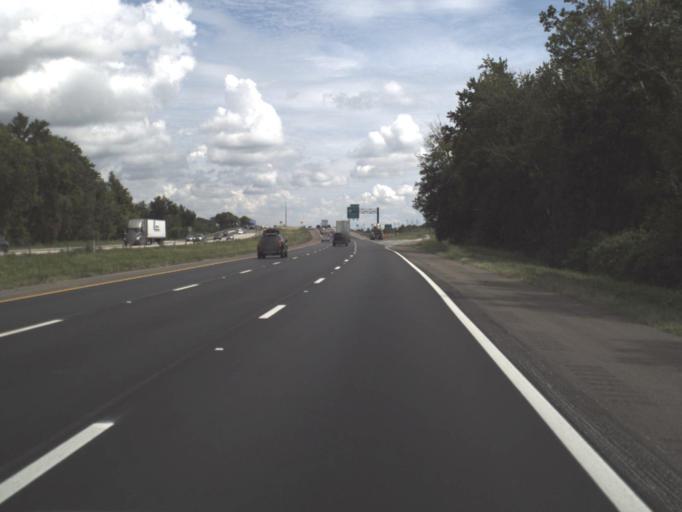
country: US
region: Florida
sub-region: Polk County
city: Loughman
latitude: 28.2567
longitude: -81.6171
